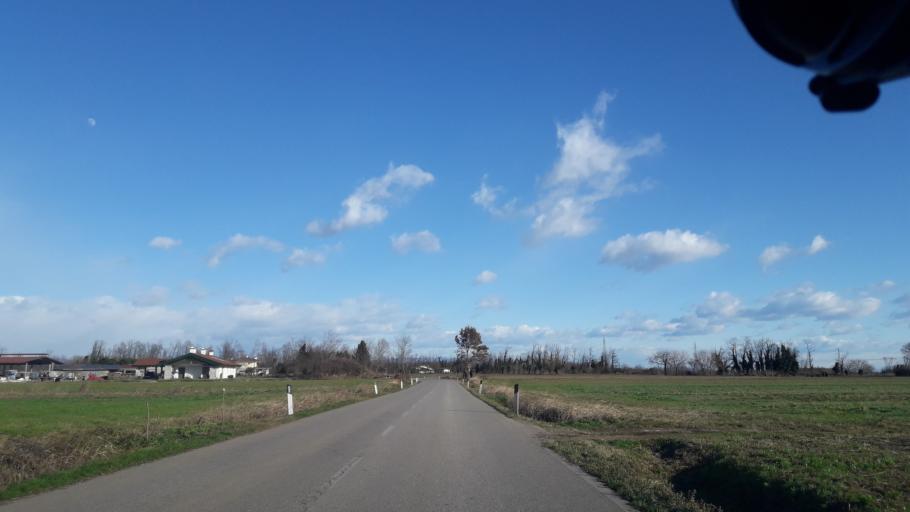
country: IT
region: Friuli Venezia Giulia
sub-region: Provincia di Udine
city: Martignacco
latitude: 46.0749
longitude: 13.1600
